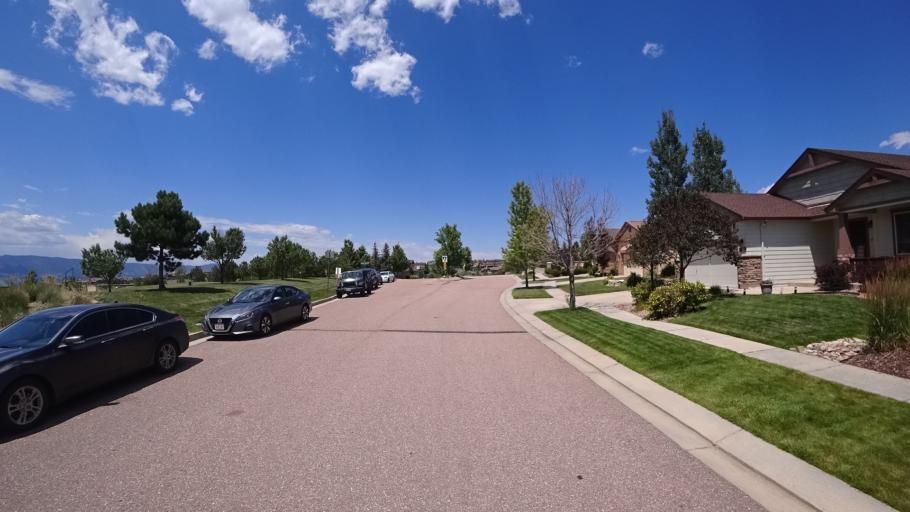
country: US
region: Colorado
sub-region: El Paso County
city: Black Forest
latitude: 38.9694
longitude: -104.7596
